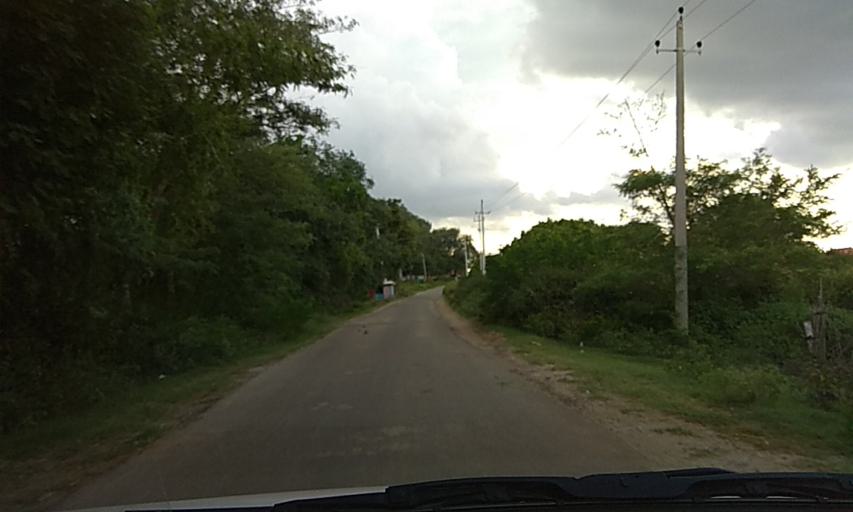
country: IN
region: Karnataka
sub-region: Chamrajnagar
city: Gundlupet
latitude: 11.8713
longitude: 76.7257
